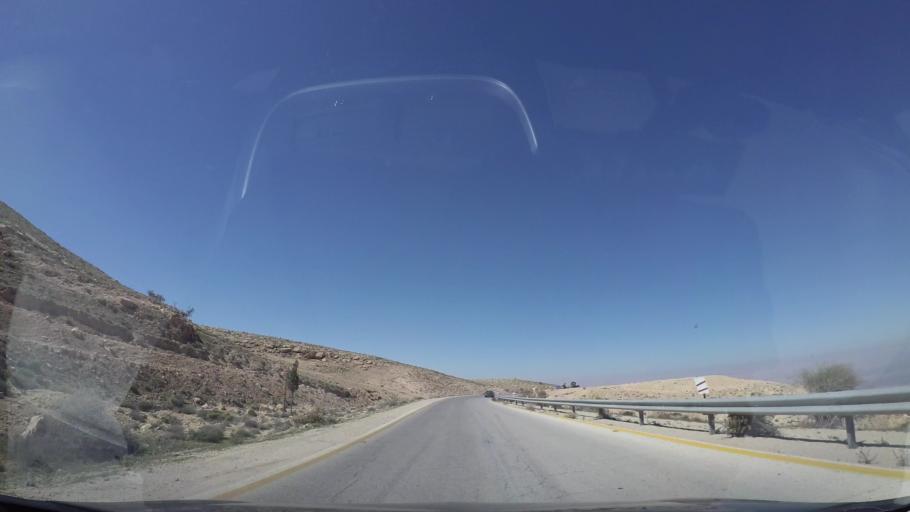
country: JO
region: Tafielah
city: At Tafilah
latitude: 30.8588
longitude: 35.5417
